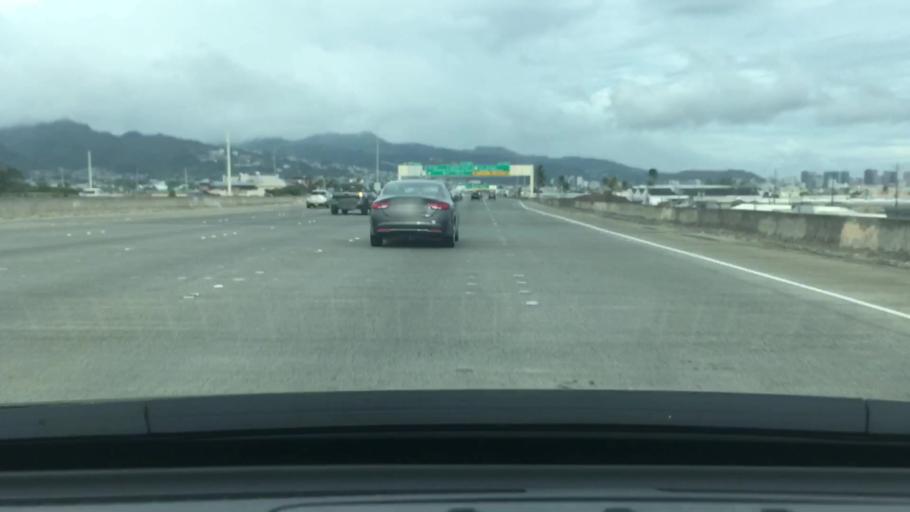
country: US
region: Hawaii
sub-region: Honolulu County
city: Halawa Heights
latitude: 21.3354
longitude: -157.9058
